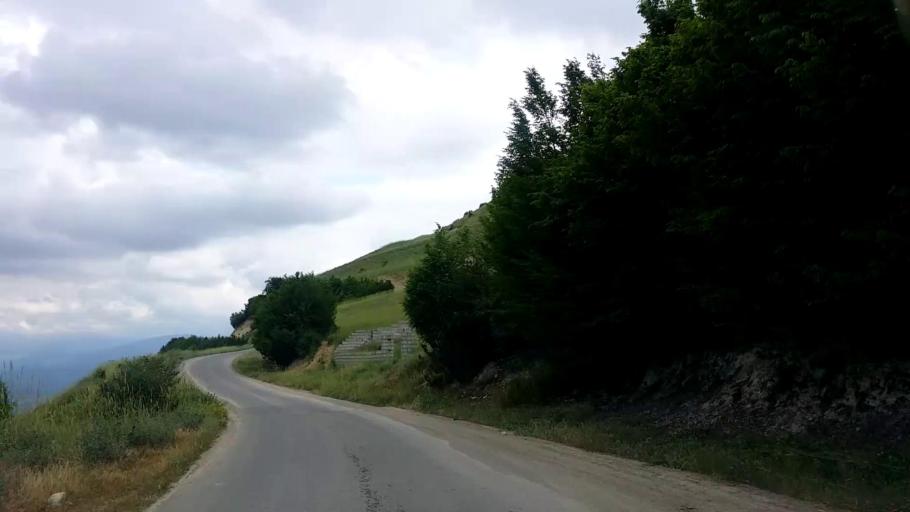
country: IR
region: Mazandaran
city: Chalus
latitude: 36.5444
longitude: 51.2712
